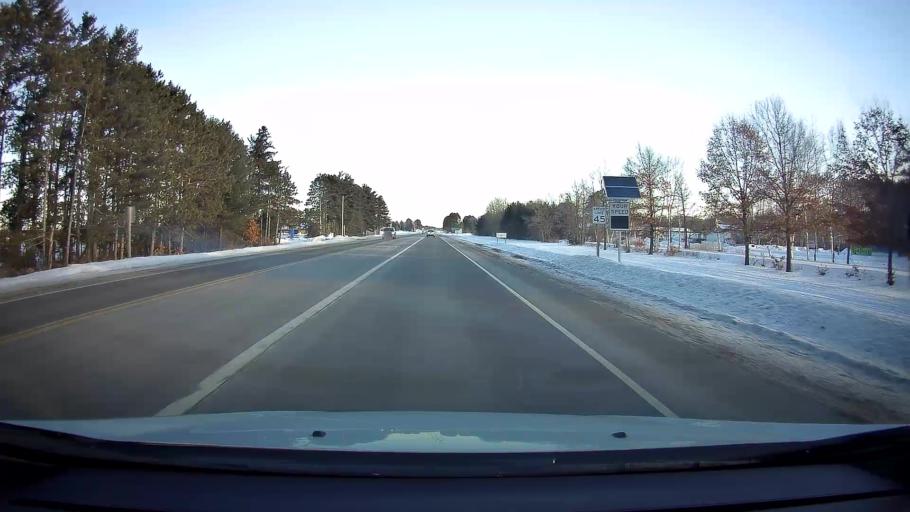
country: US
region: Wisconsin
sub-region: Washburn County
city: Shell Lake
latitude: 45.7287
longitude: -91.9325
